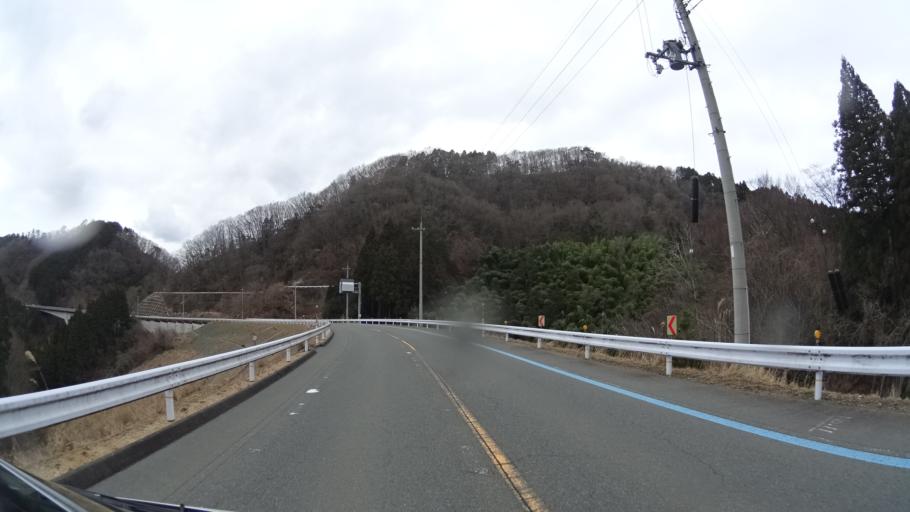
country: JP
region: Kyoto
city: Maizuru
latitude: 35.4328
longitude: 135.4094
